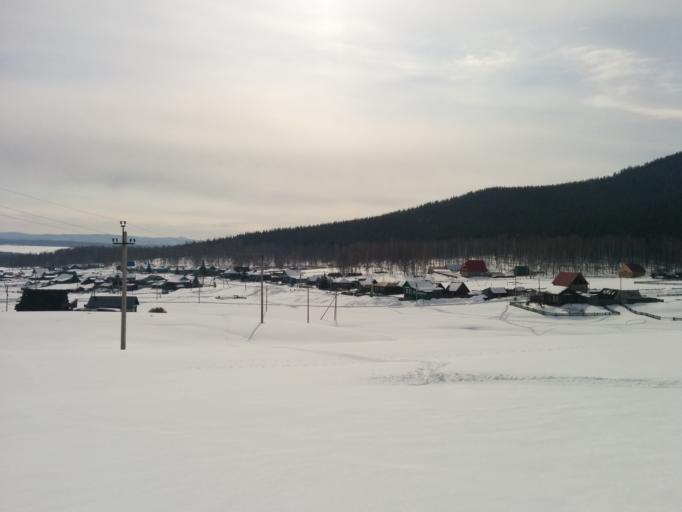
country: RU
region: Bashkortostan
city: Lomovka
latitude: 53.8061
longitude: 58.1953
